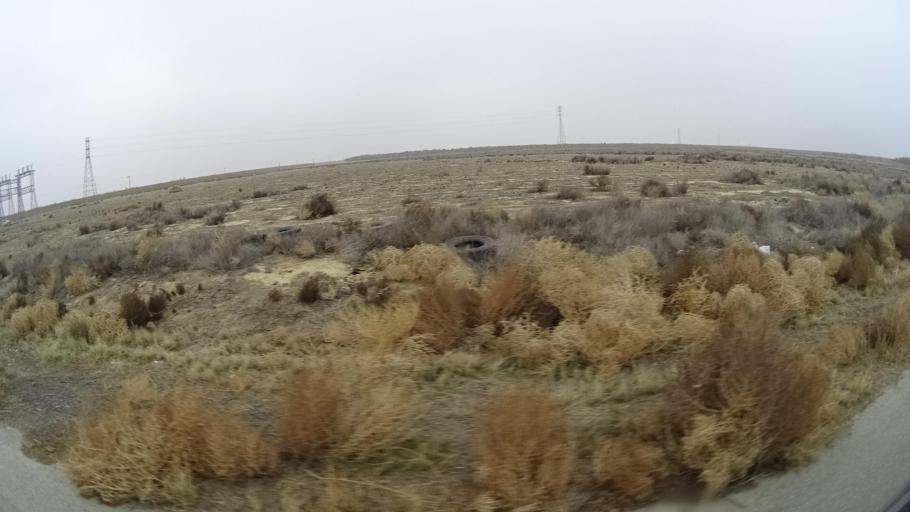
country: US
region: California
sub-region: Kern County
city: Lost Hills
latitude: 35.6012
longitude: -119.5786
